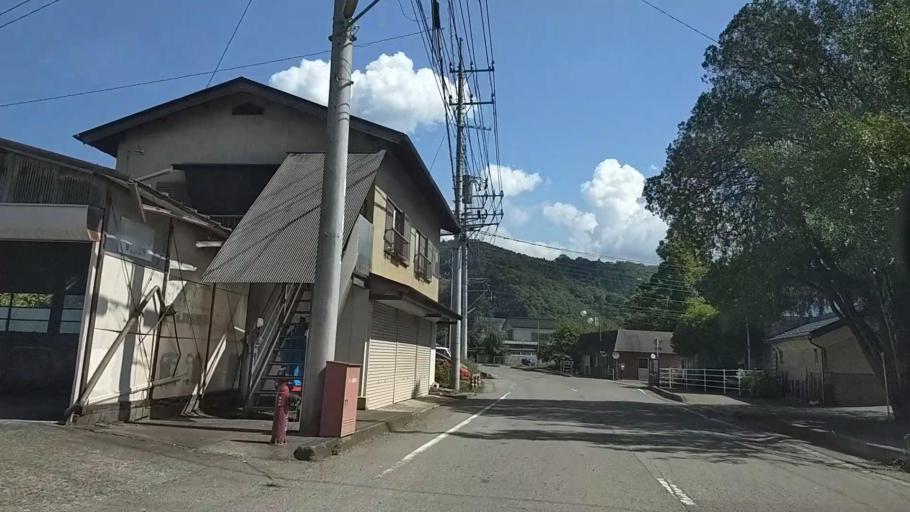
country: JP
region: Yamanashi
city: Ryuo
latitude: 35.4610
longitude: 138.4454
